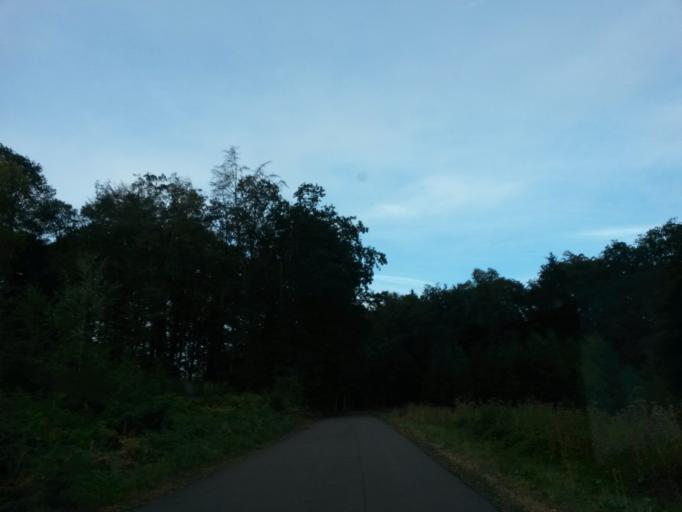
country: DE
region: North Rhine-Westphalia
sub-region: Regierungsbezirk Koln
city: Gummersbach
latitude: 51.0343
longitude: 7.5975
